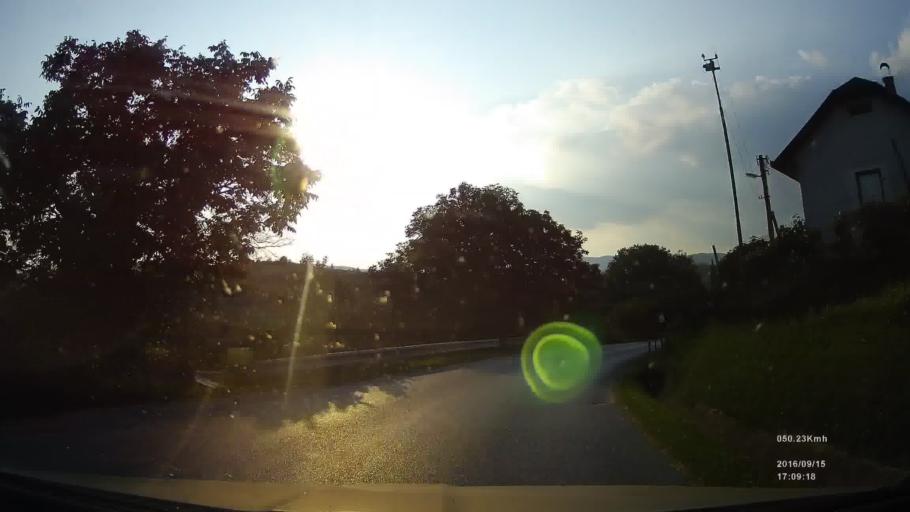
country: SK
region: Presovsky
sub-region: Okres Presov
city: Presov
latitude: 48.9150
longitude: 21.1250
